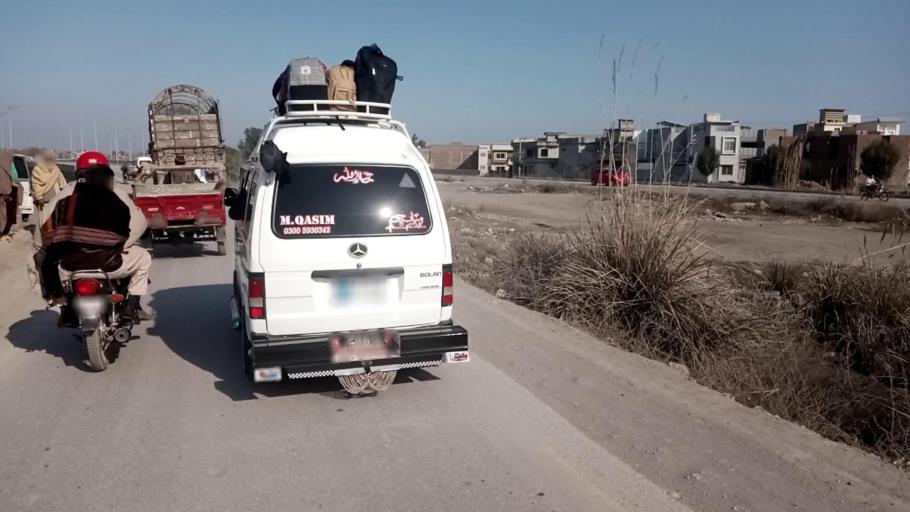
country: PK
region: Khyber Pakhtunkhwa
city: Peshawar
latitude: 34.0367
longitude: 71.5318
